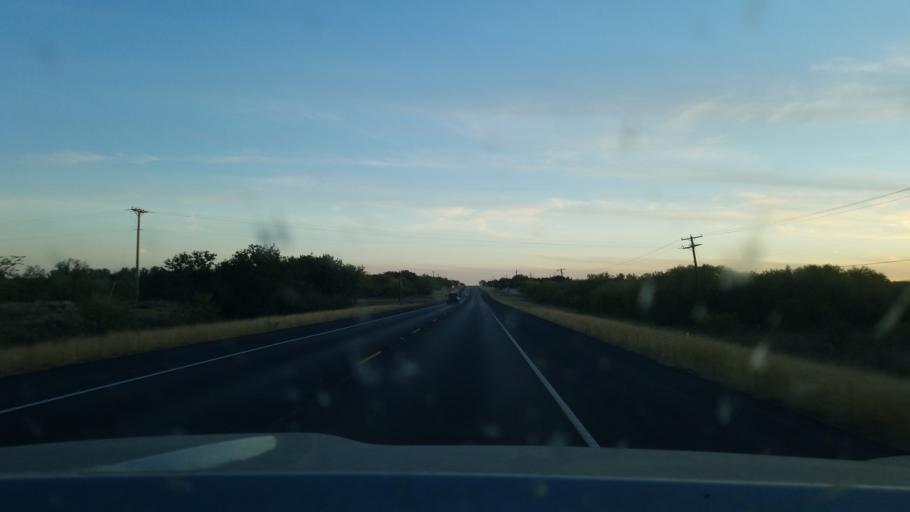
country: US
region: Texas
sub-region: Stephens County
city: Breckenridge
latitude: 32.6921
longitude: -98.9026
